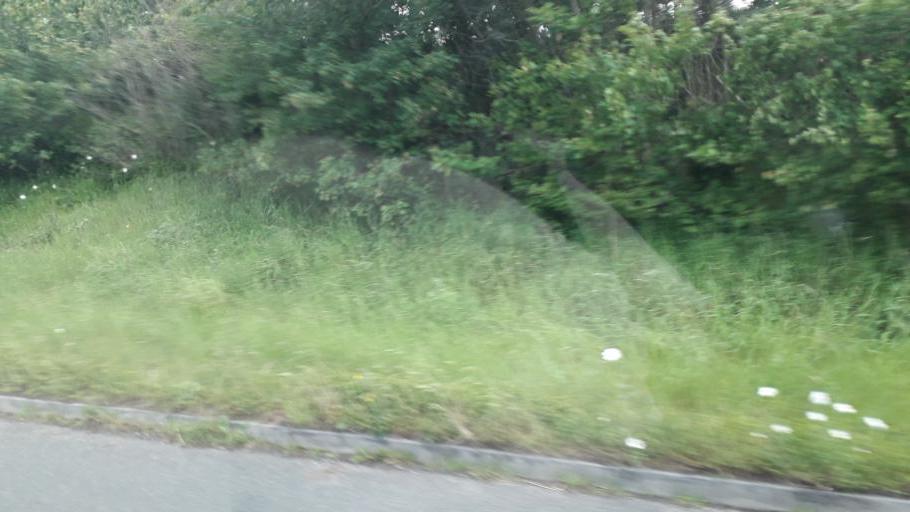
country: IE
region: Leinster
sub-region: Kildare
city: Moone
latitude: 53.0073
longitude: -6.8039
